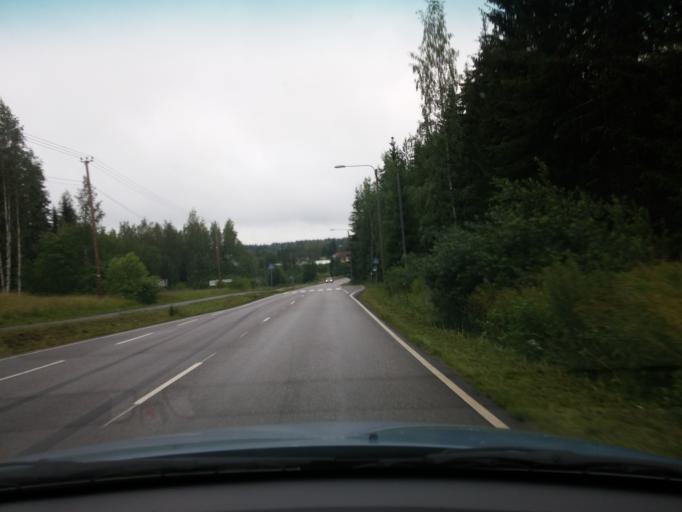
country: FI
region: Uusimaa
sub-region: Helsinki
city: Nurmijaervi
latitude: 60.3592
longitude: 24.7447
